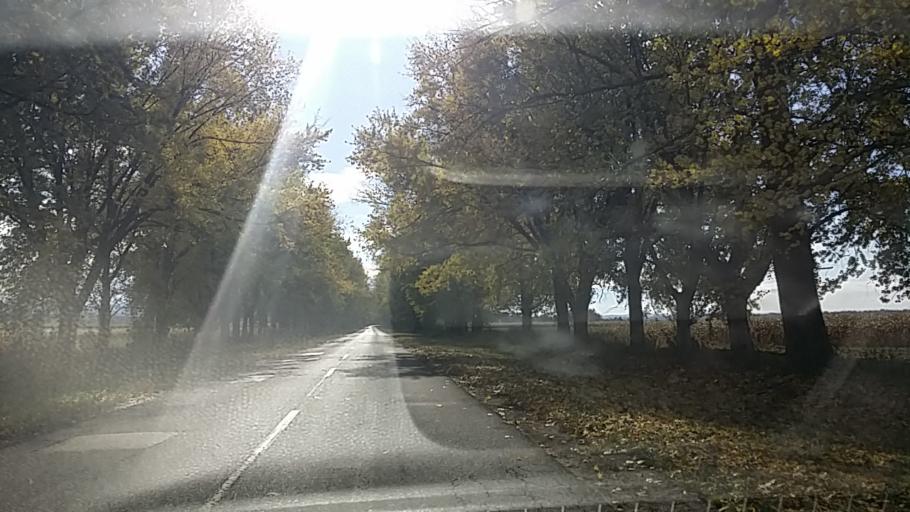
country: HU
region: Borsod-Abauj-Zemplen
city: Gonc
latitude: 48.4311
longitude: 21.2381
